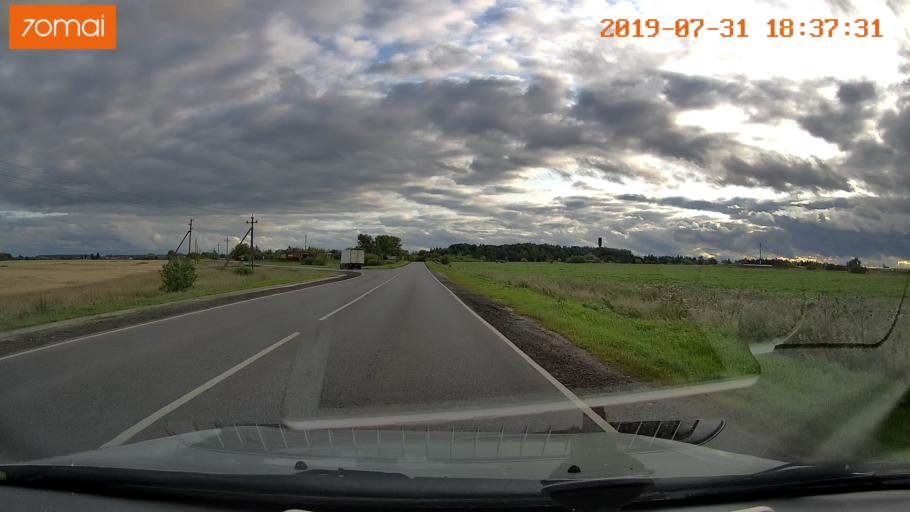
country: RU
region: Moskovskaya
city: Voskresensk
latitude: 55.2784
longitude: 38.6603
